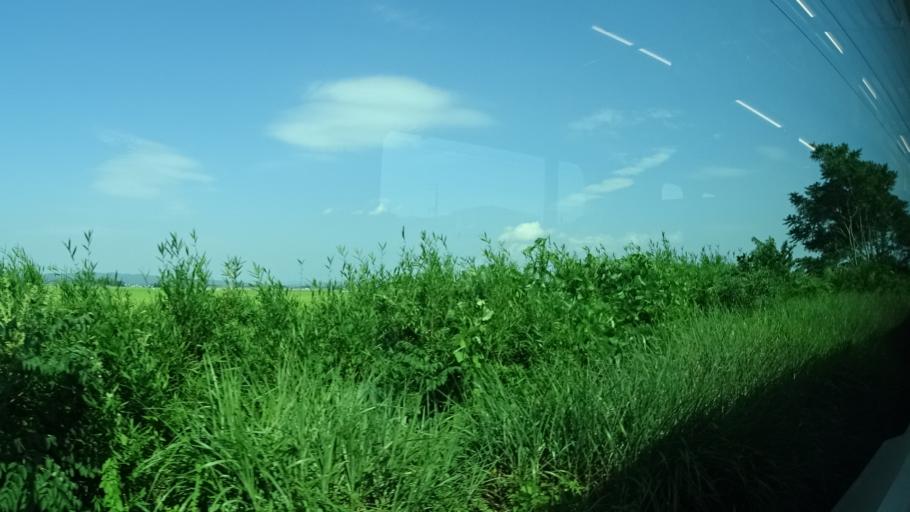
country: JP
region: Miyagi
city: Kogota
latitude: 38.5118
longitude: 141.0758
